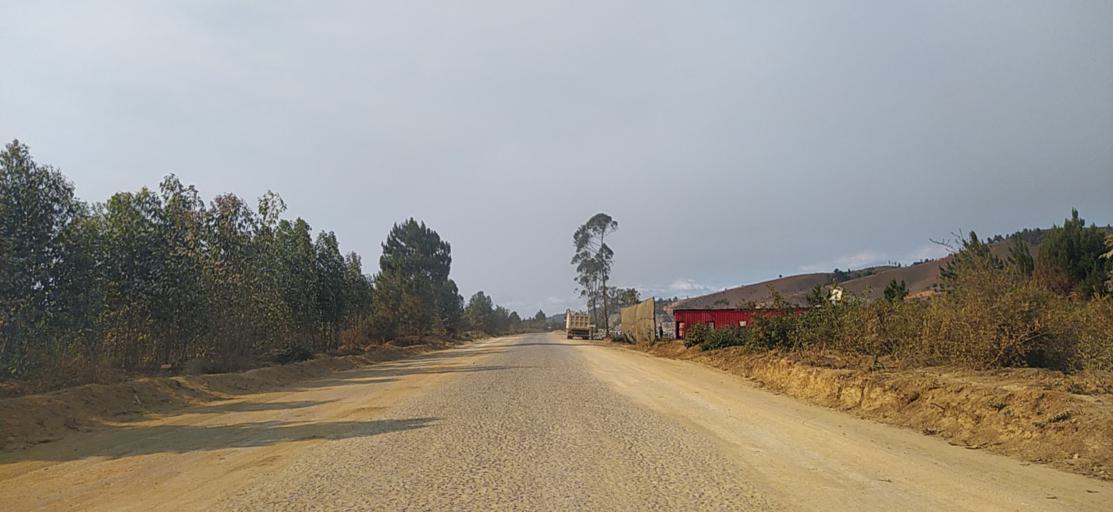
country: MG
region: Alaotra Mangoro
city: Moramanga
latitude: -18.6708
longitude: 48.2738
